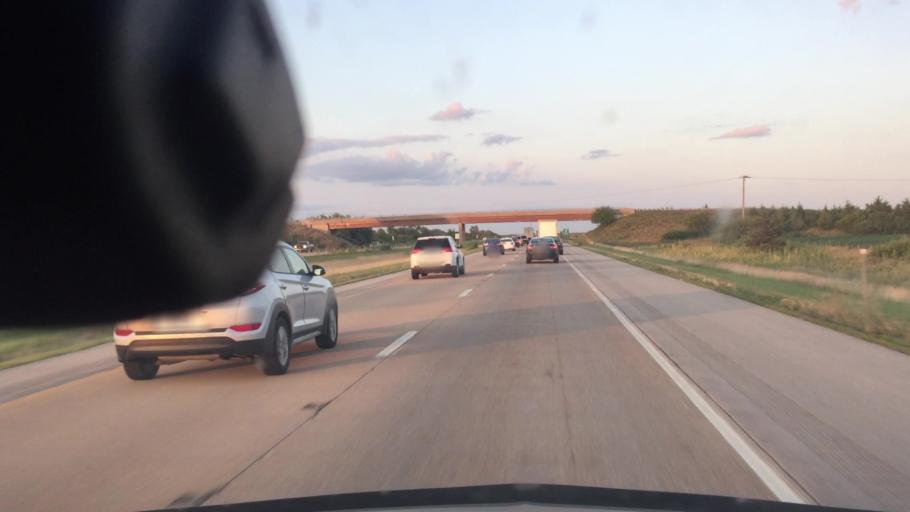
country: US
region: Illinois
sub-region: Livingston County
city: Dwight
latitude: 41.1135
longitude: -88.4354
